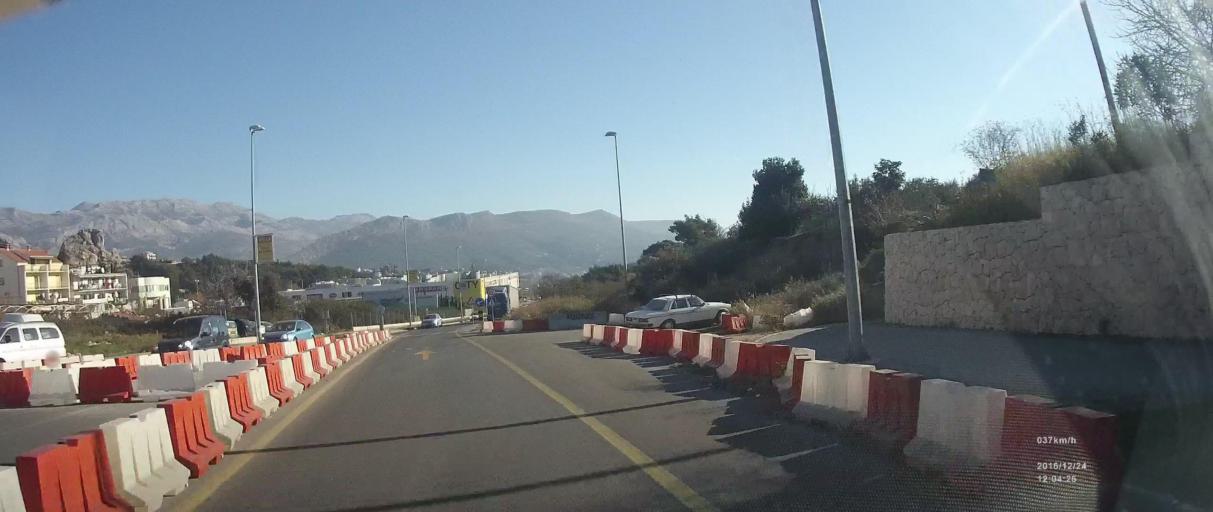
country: HR
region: Splitsko-Dalmatinska
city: Kamen
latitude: 43.5140
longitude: 16.4974
